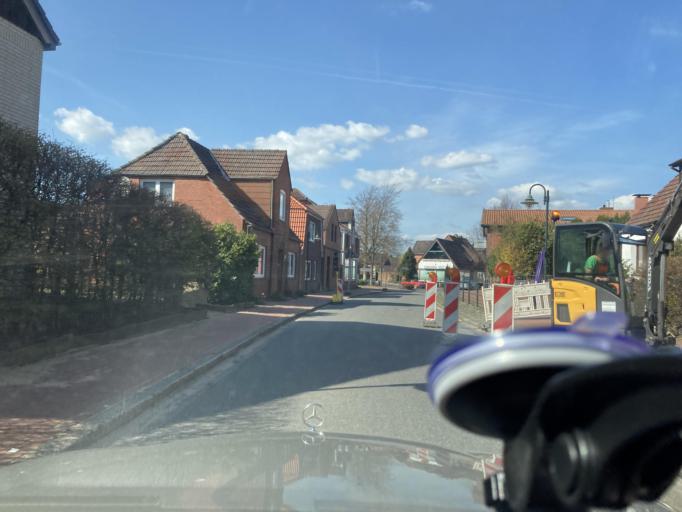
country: DE
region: Schleswig-Holstein
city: Lehe
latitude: 54.3295
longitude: 9.0223
